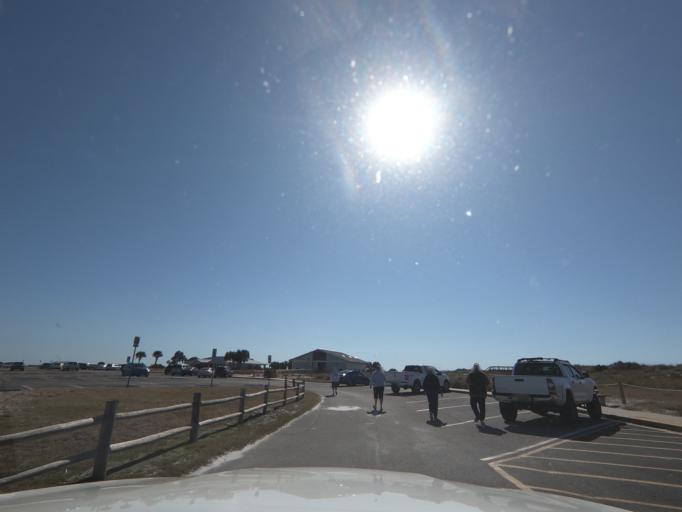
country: US
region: Florida
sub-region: Bay County
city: Lower Grand Lagoon
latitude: 30.1256
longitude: -85.7349
